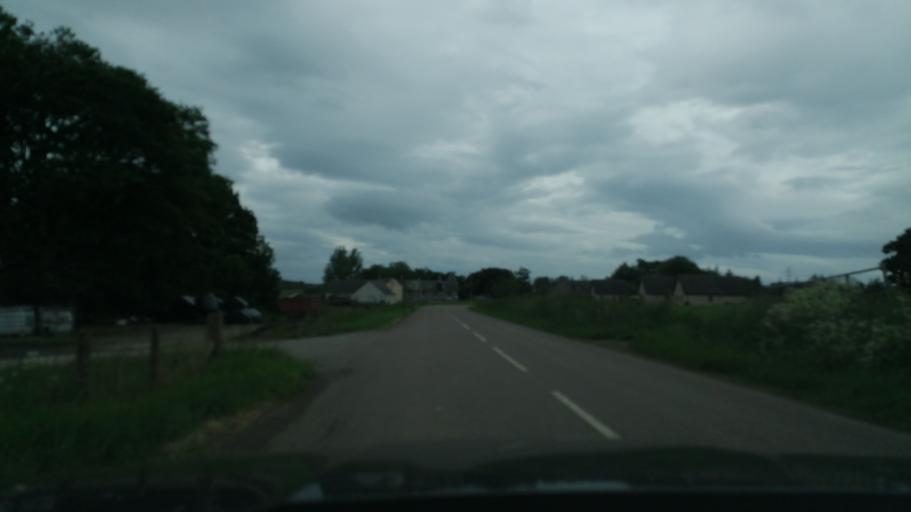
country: GB
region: Scotland
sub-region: Moray
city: Keith
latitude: 57.5795
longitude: -2.8706
